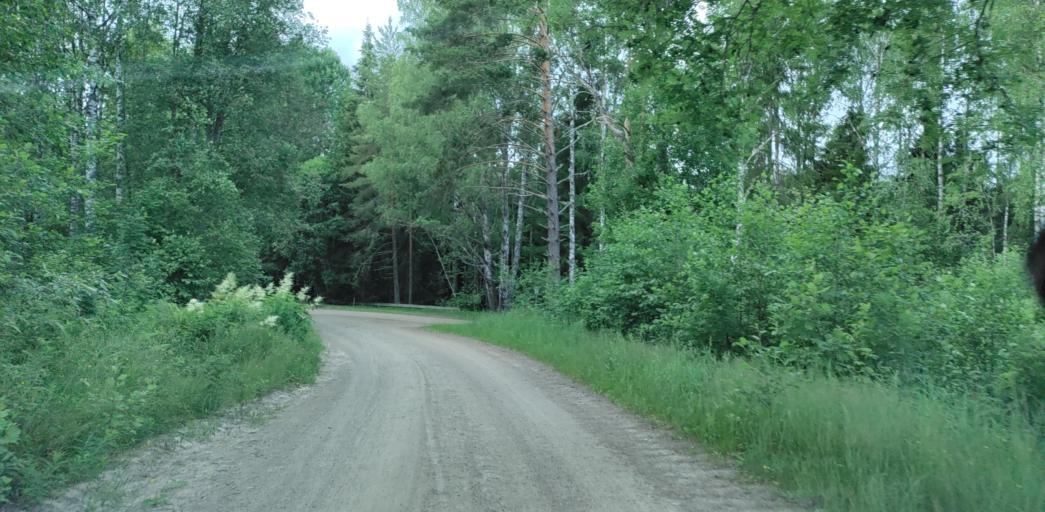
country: SE
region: Vaermland
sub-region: Hagfors Kommun
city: Hagfors
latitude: 60.0599
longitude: 13.5767
